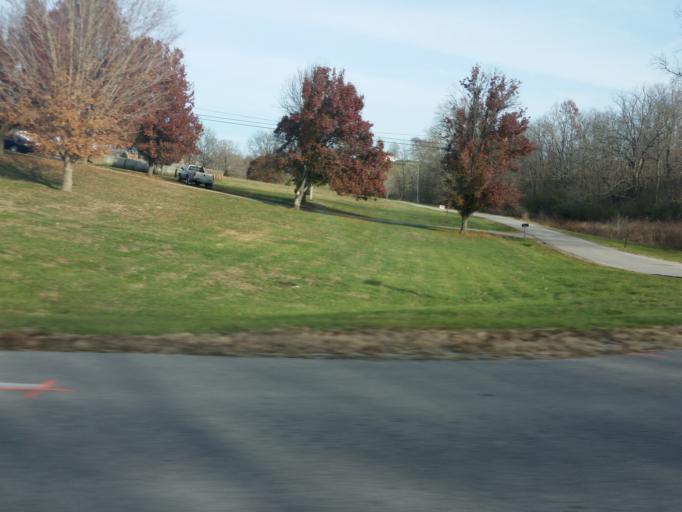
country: US
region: Kentucky
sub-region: Harrison County
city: Cynthiana
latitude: 38.4515
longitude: -84.2842
